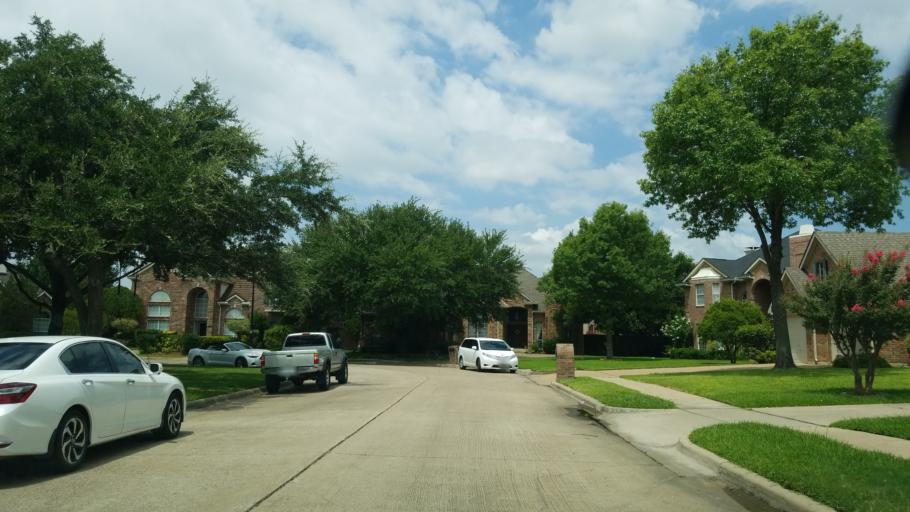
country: US
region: Texas
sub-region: Dallas County
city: Coppell
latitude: 32.9367
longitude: -96.9611
